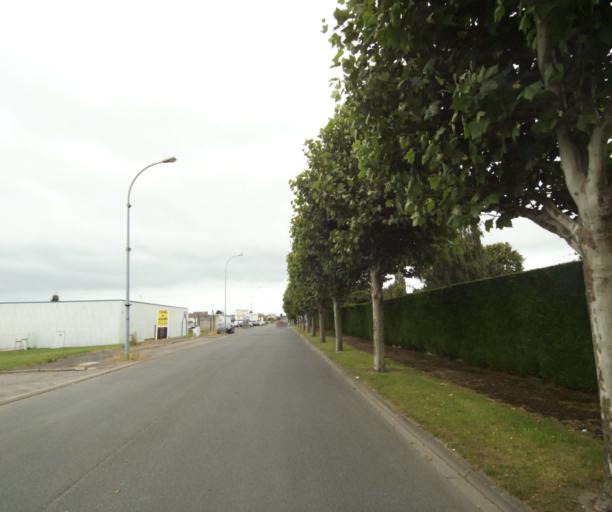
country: FR
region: Lower Normandy
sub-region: Departement du Calvados
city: Dives-sur-Mer
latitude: 49.2781
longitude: -0.1000
